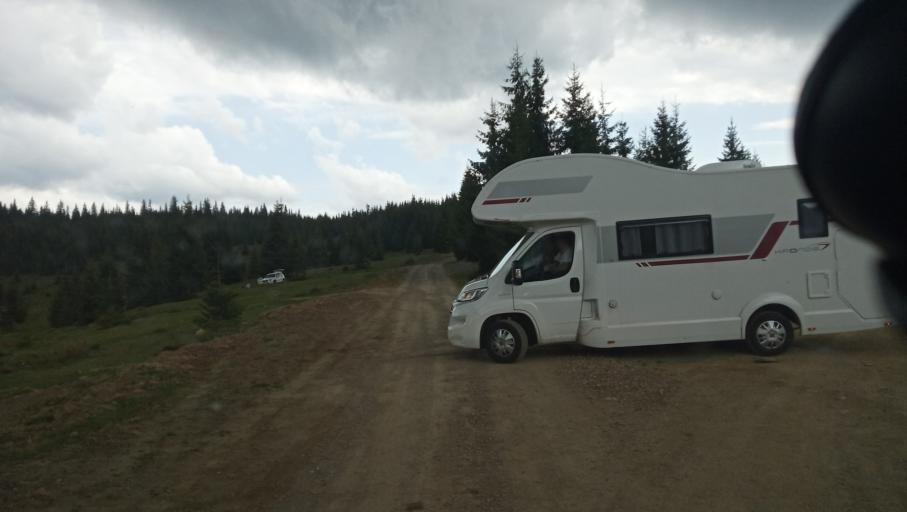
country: RO
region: Cluj
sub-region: Comuna Belis
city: Belis
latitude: 46.6280
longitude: 23.0443
